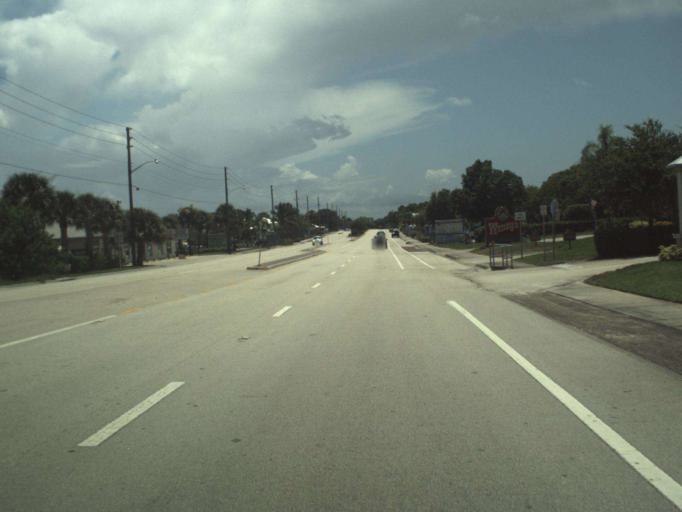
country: US
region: Florida
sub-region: Indian River County
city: Sebastian
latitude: 27.8243
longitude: -80.4748
